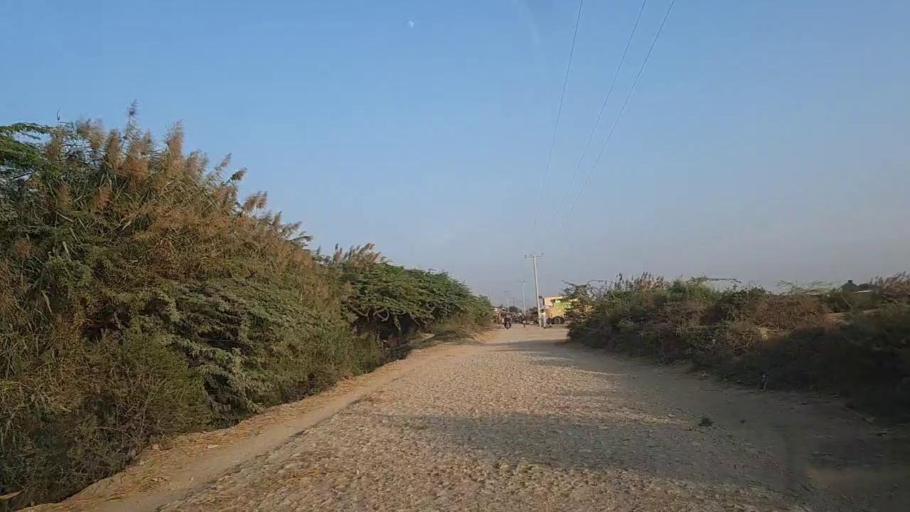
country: PK
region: Sindh
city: Keti Bandar
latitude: 24.2743
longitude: 67.6711
